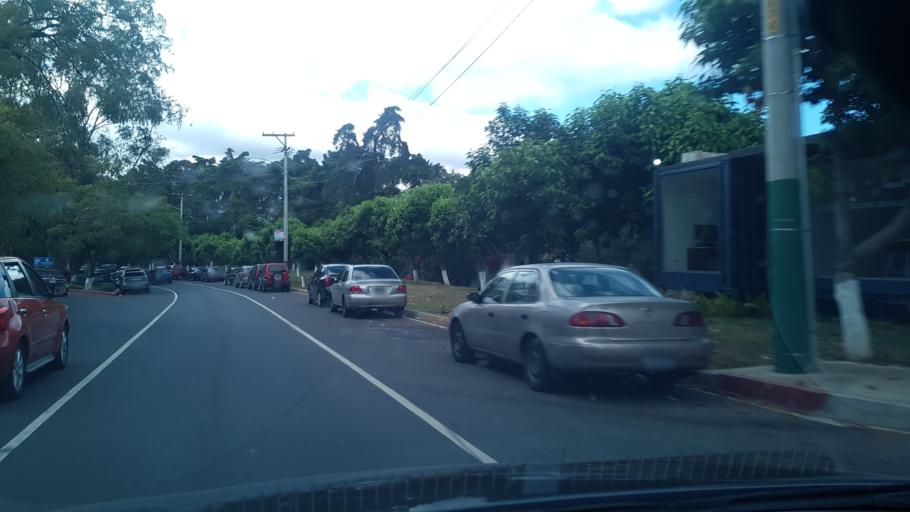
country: GT
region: Guatemala
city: Santa Catarina Pinula
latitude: 14.5894
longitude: -90.5525
